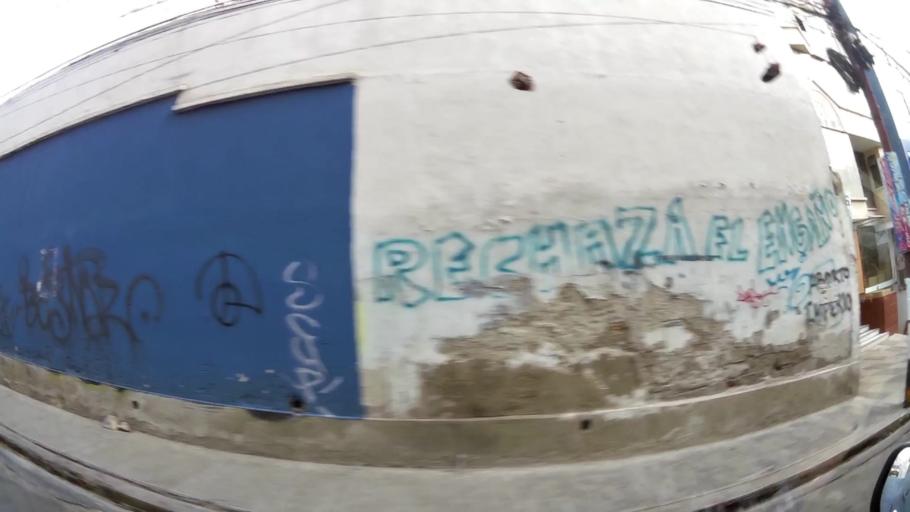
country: BO
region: La Paz
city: La Paz
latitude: -16.4962
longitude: -68.1313
